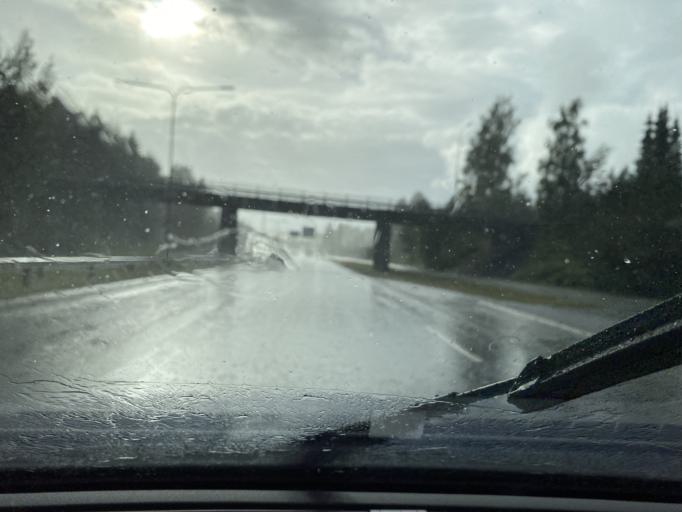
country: FI
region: Uusimaa
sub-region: Helsinki
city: Nurmijaervi
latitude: 60.4568
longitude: 24.8378
